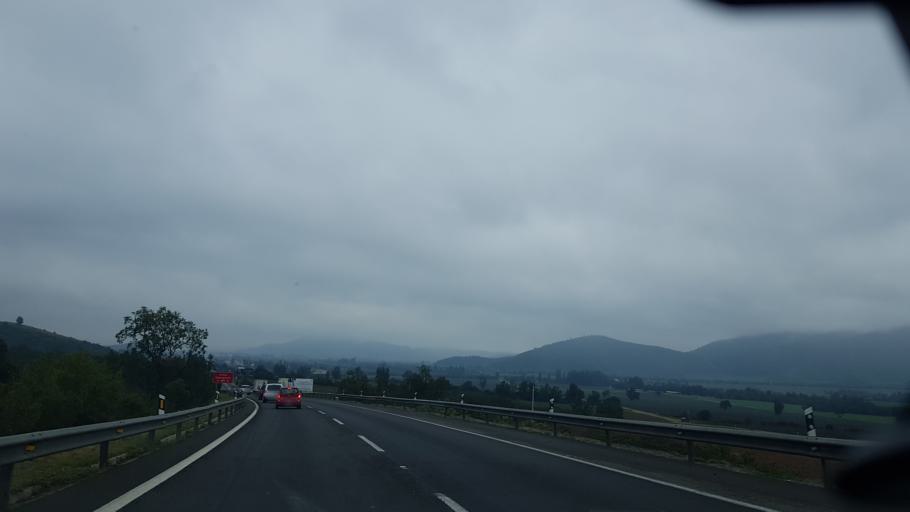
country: CL
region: Santiago Metropolitan
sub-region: Provincia de Melipilla
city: Melipilla
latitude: -33.3804
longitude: -71.2782
